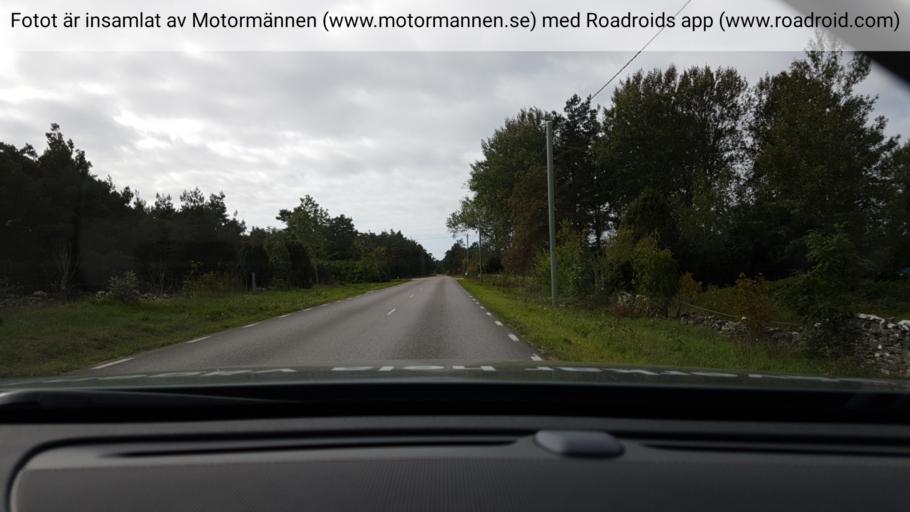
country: SE
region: Gotland
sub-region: Gotland
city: Hemse
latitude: 56.9608
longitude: 18.2212
